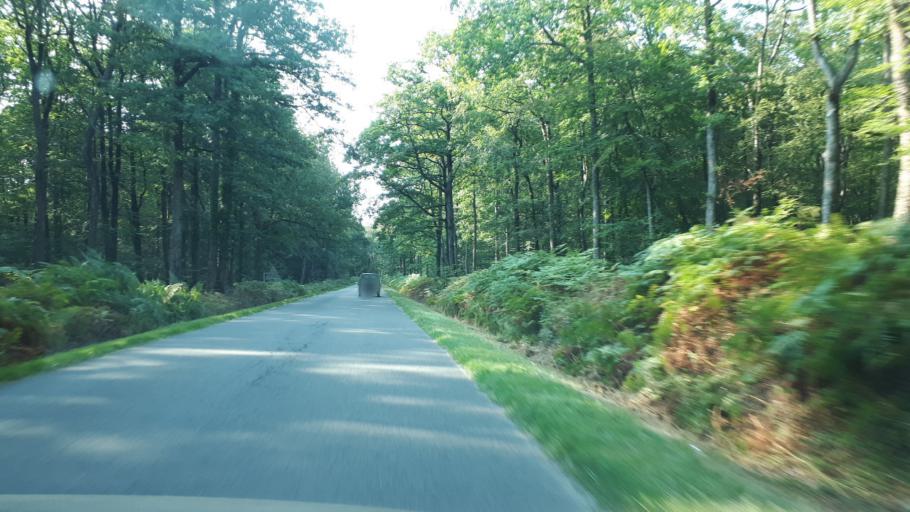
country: FR
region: Centre
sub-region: Departement du Cher
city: Saint-Eloy-de-Gy
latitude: 47.2198
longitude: 2.3490
